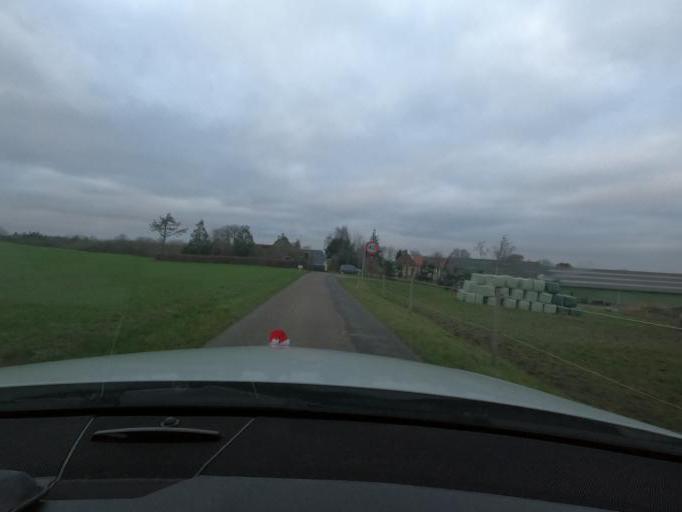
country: DK
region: South Denmark
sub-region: Sonderborg Kommune
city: Sonderborg
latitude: 54.9042
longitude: 9.8500
